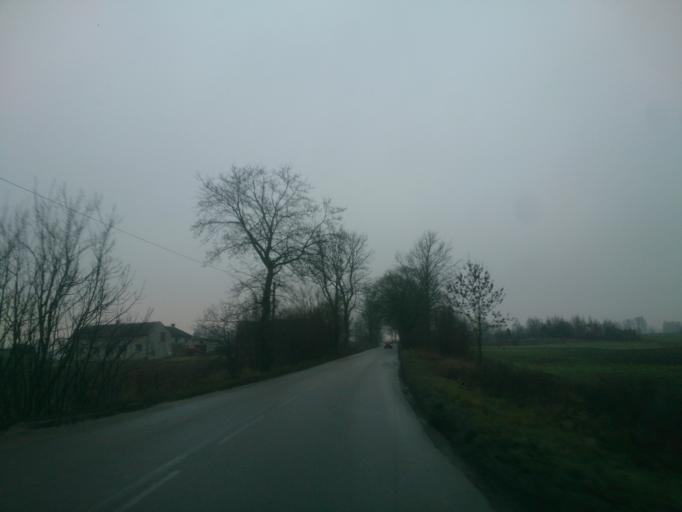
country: PL
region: Pomeranian Voivodeship
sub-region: Powiat koscierski
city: Stara Kiszewa
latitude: 54.0246
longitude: 18.0945
